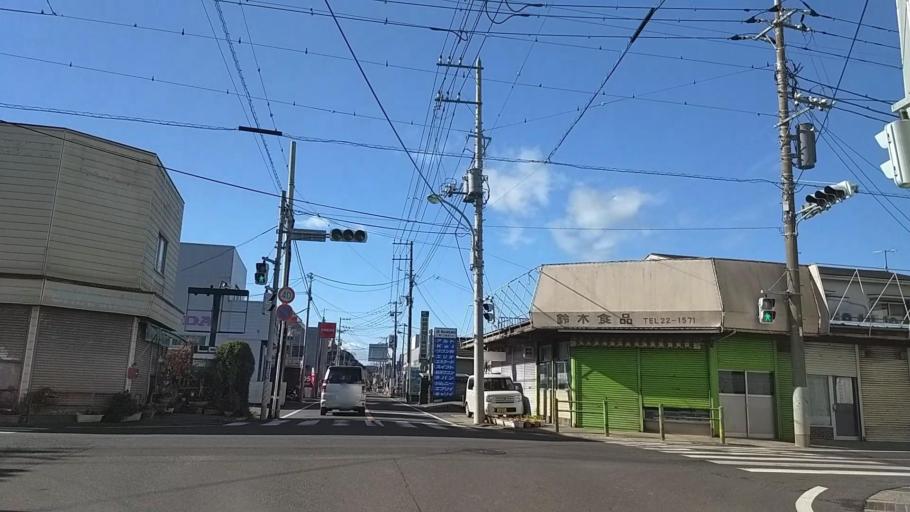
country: JP
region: Chiba
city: Tateyama
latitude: 34.9847
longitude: 139.8610
